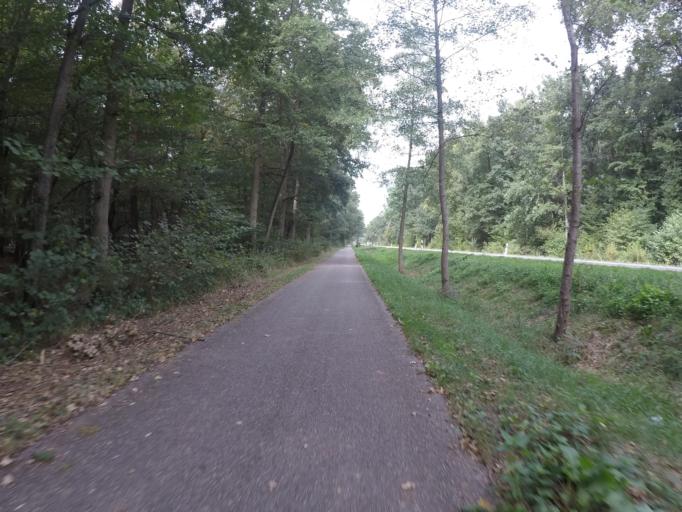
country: DE
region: Rheinland-Pfalz
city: Hanhofen
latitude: 49.3515
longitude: 8.3498
